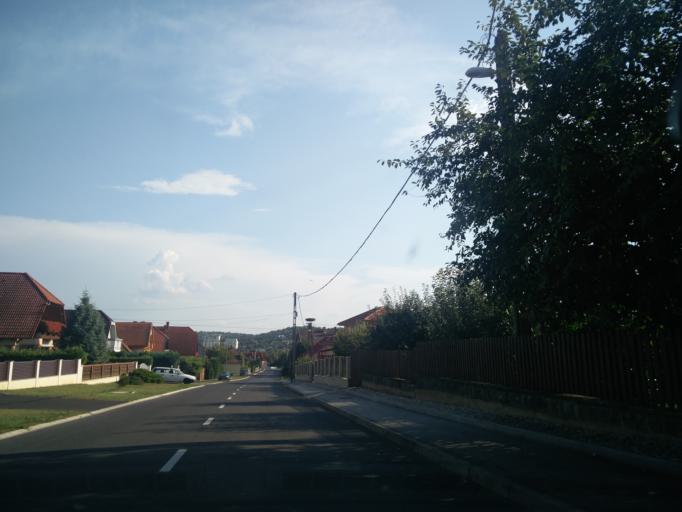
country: HU
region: Zala
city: Zalaegerszeg
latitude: 46.8646
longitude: 16.8069
